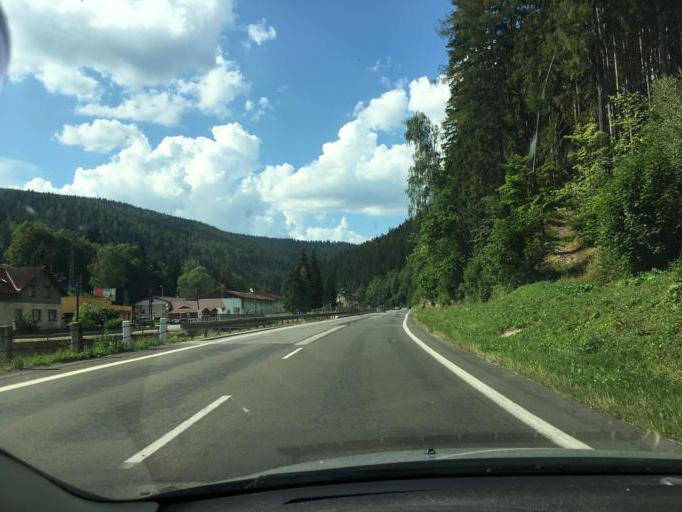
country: CZ
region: Kralovehradecky
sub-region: Okres Trutnov
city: Vrchlabi
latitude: 50.6578
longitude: 15.6005
